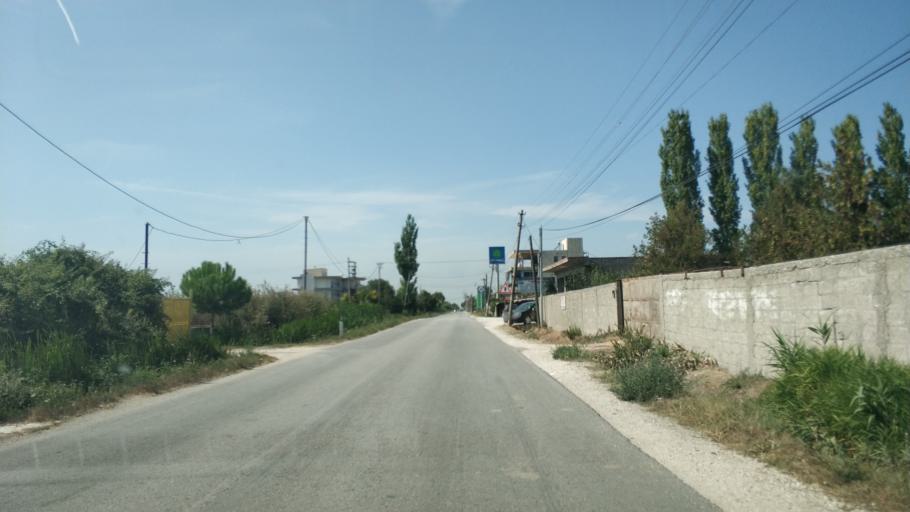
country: AL
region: Fier
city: Fier
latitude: 40.7314
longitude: 19.5379
